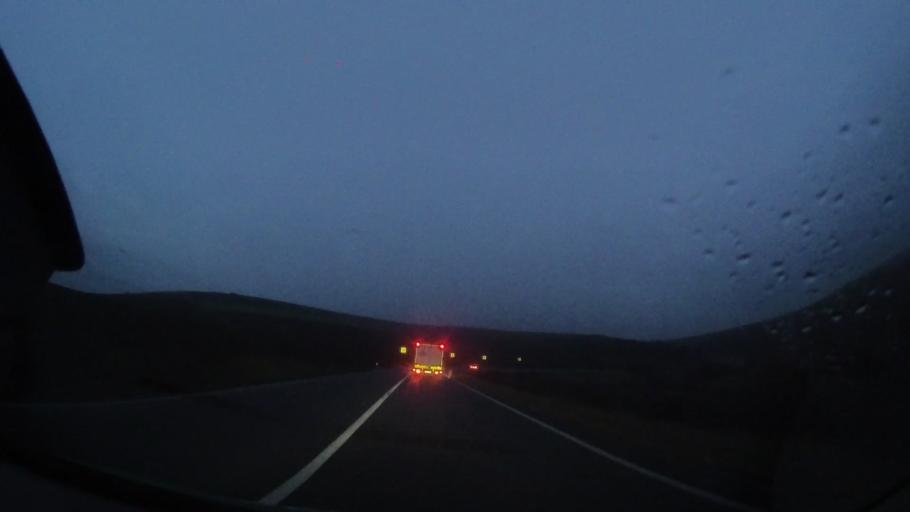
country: RO
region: Harghita
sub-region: Comuna Ditrau
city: Ditrau
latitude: 46.8378
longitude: 25.4866
